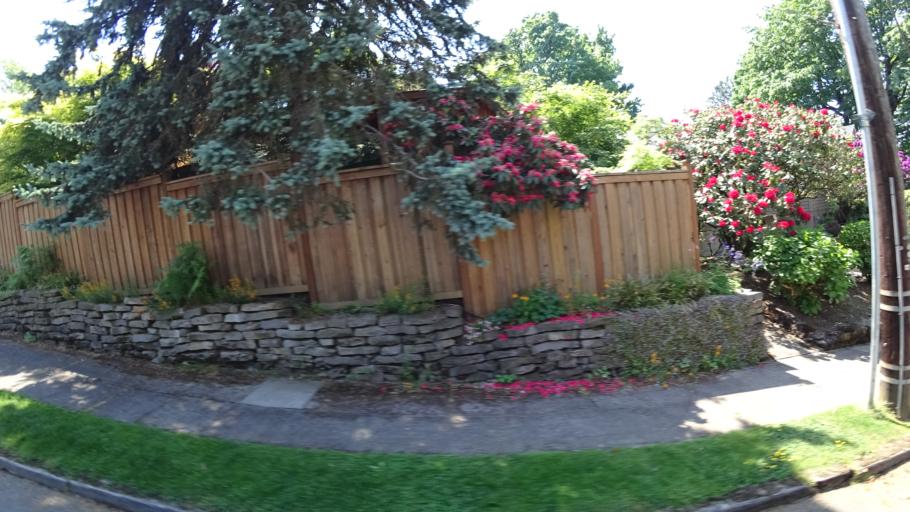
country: US
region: Oregon
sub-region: Multnomah County
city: Portland
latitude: 45.4947
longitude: -122.7009
